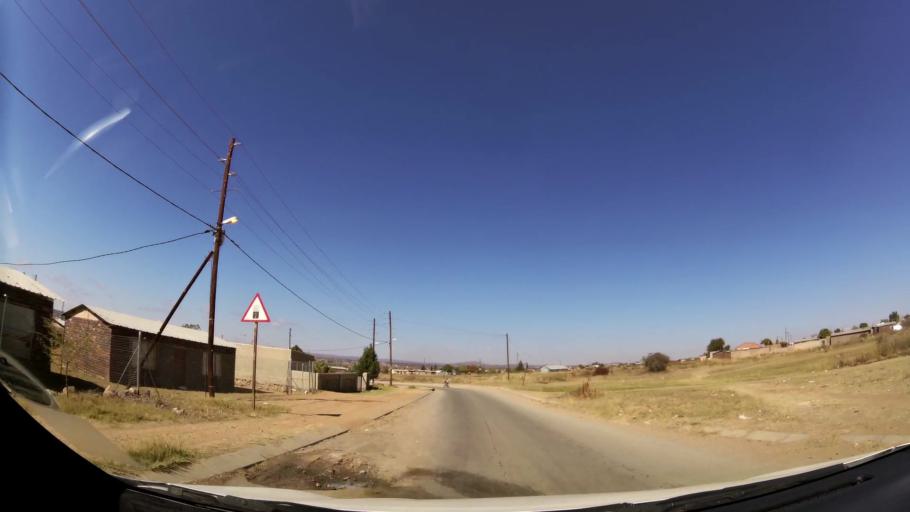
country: ZA
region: Limpopo
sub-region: Capricorn District Municipality
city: Polokwane
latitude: -23.8856
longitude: 29.4095
